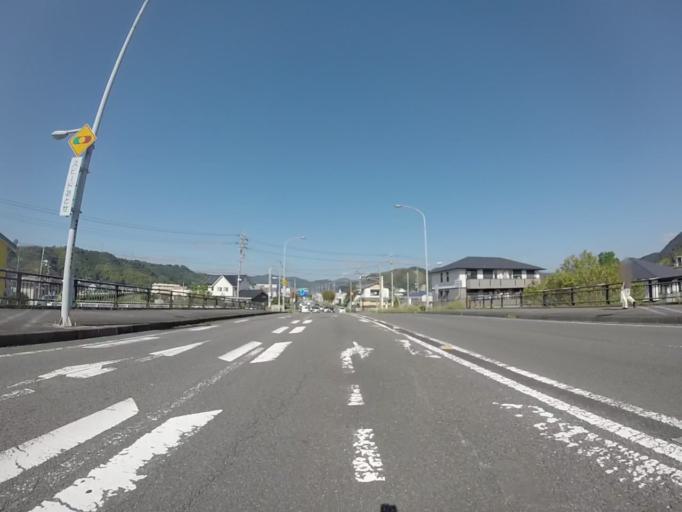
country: JP
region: Shizuoka
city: Fujieda
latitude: 34.8849
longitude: 138.2628
